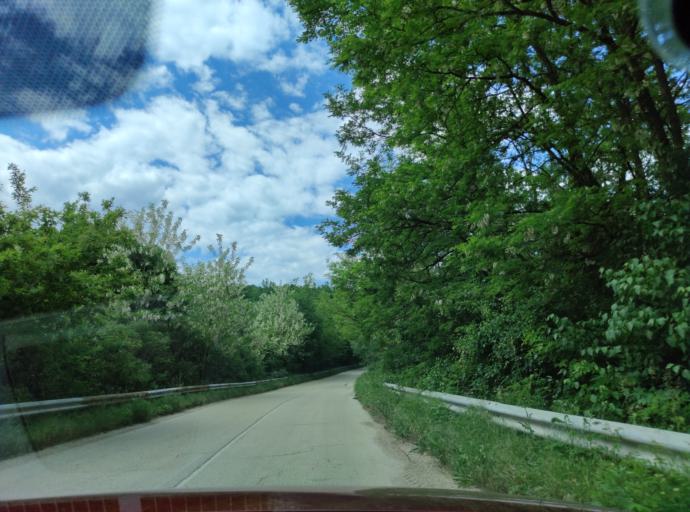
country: BG
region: Montana
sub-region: Obshtina Berkovitsa
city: Berkovitsa
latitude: 43.3750
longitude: 23.0769
